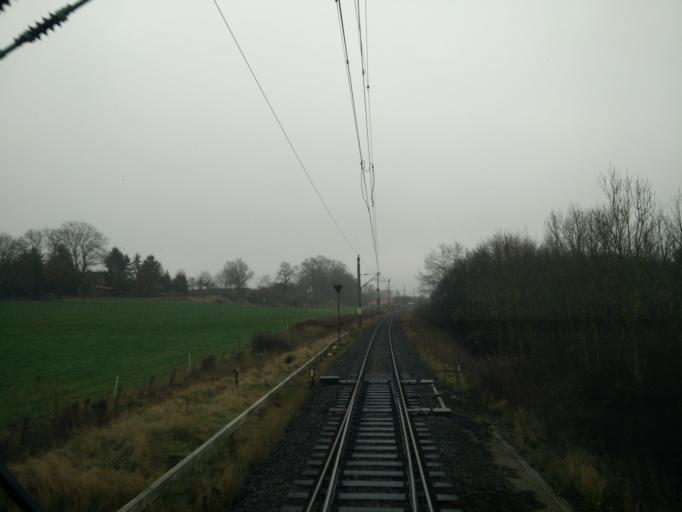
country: DE
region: Mecklenburg-Vorpommern
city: Mecklenburg
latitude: 53.8399
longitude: 11.4744
